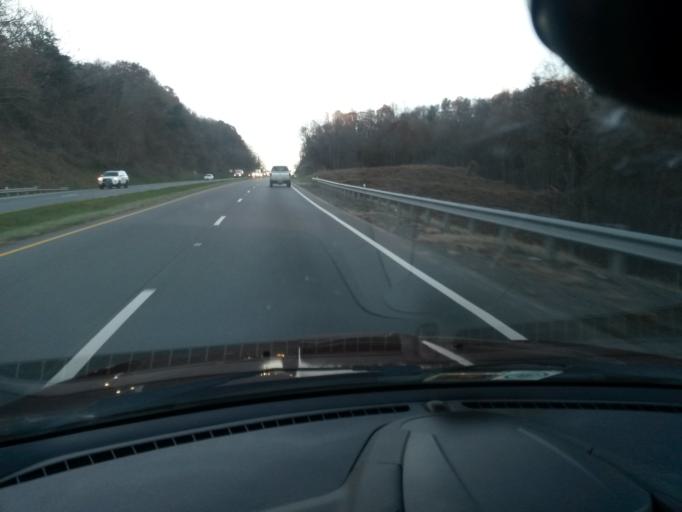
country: US
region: Virginia
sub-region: Roanoke County
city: Narrows
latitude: 37.1024
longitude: -79.9420
